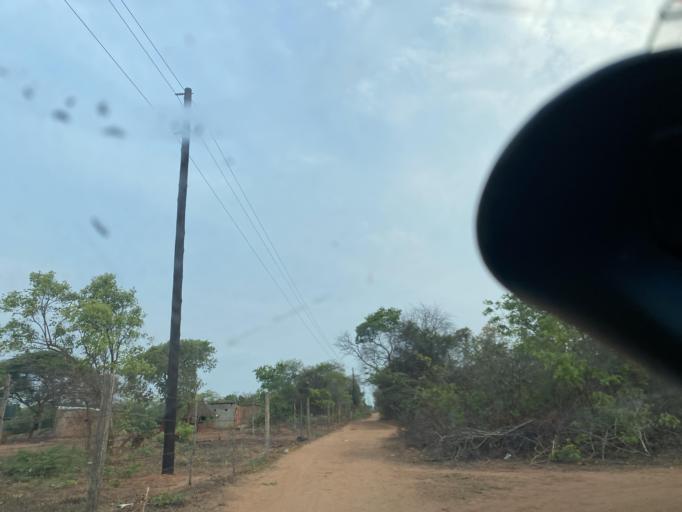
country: ZM
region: Lusaka
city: Chongwe
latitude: -15.1988
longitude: 28.4943
